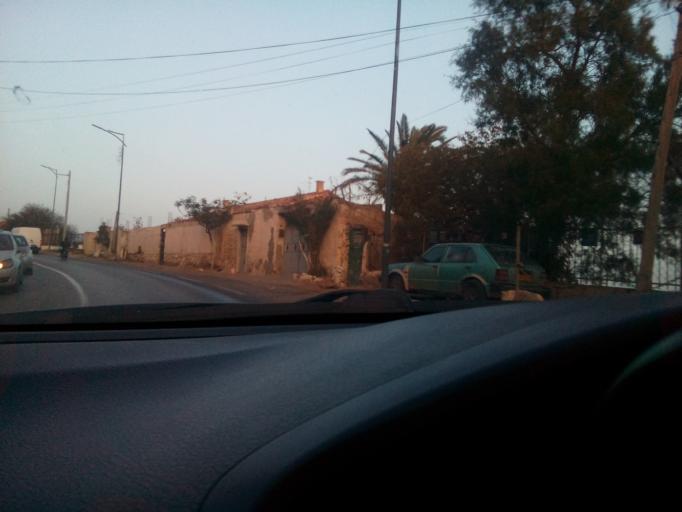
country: DZ
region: Oran
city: Oran
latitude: 35.7142
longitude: -0.6636
